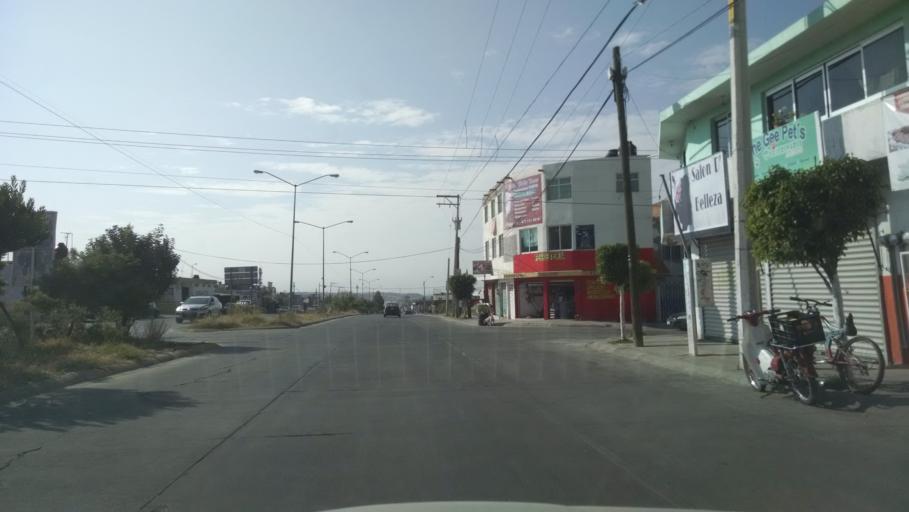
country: MX
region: Guanajuato
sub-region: Leon
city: La Ermita
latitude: 21.1554
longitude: -101.7370
